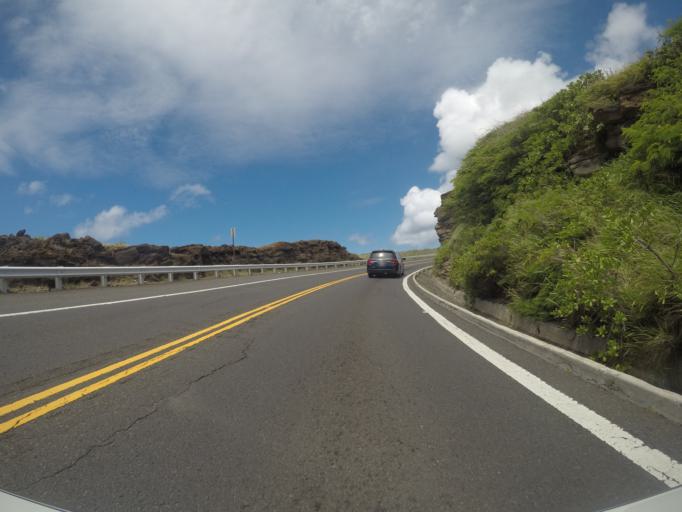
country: US
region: Hawaii
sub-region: Honolulu County
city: Waimanalo Beach
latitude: 21.2732
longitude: -157.6887
